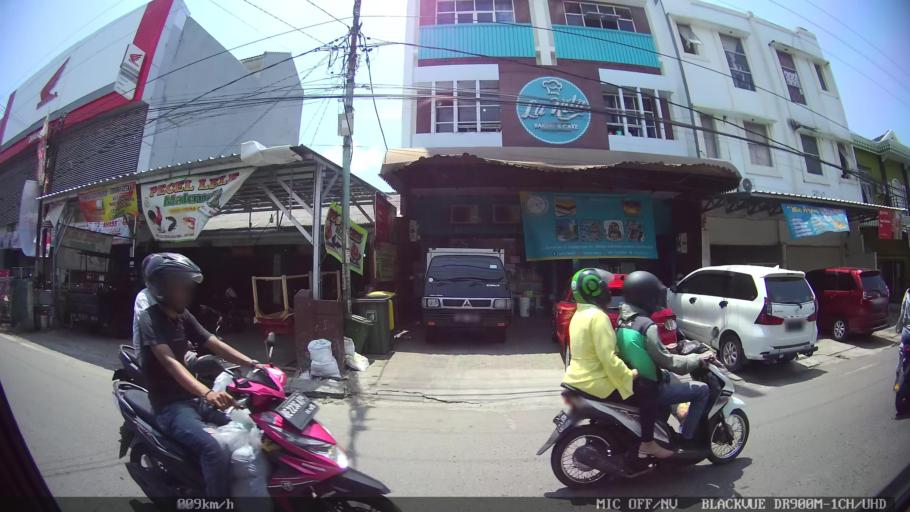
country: ID
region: Lampung
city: Kedaton
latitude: -5.3778
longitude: 105.2723
